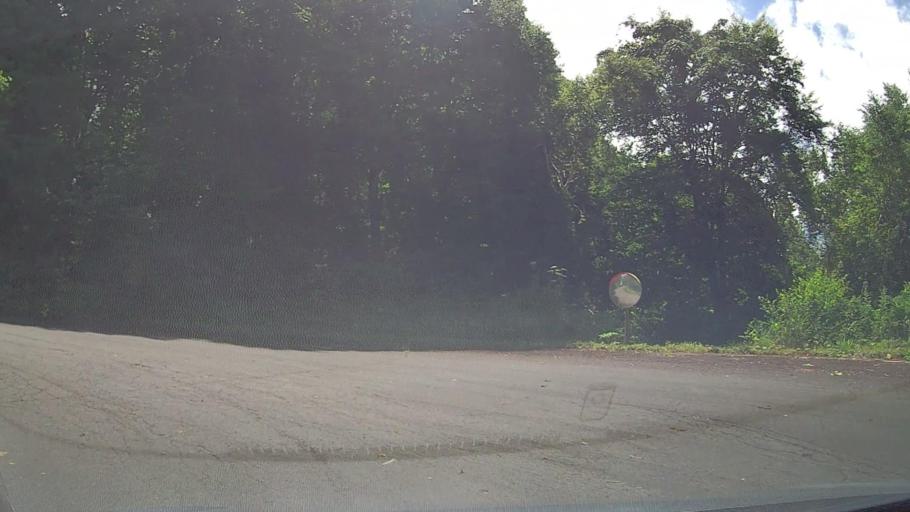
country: JP
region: Nagano
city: Iiyama
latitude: 36.9213
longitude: 138.4757
